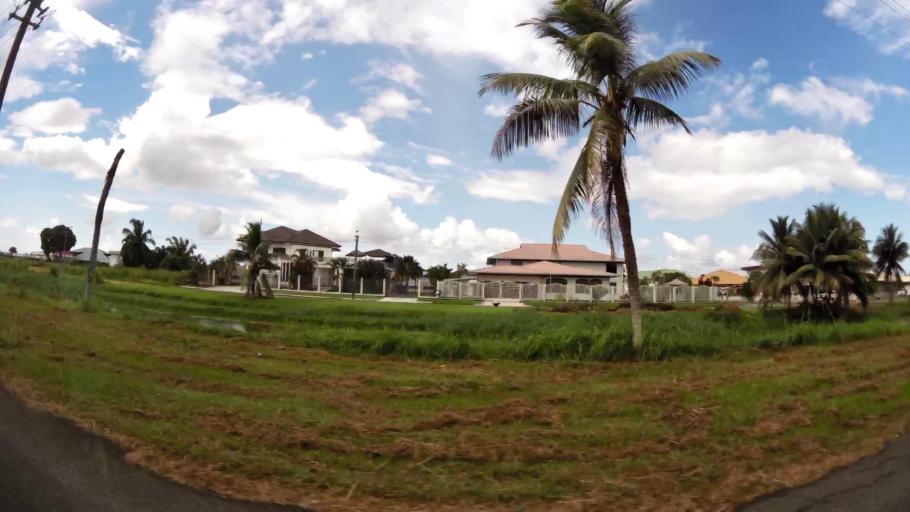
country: SR
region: Paramaribo
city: Paramaribo
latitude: 5.8383
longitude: -55.1259
